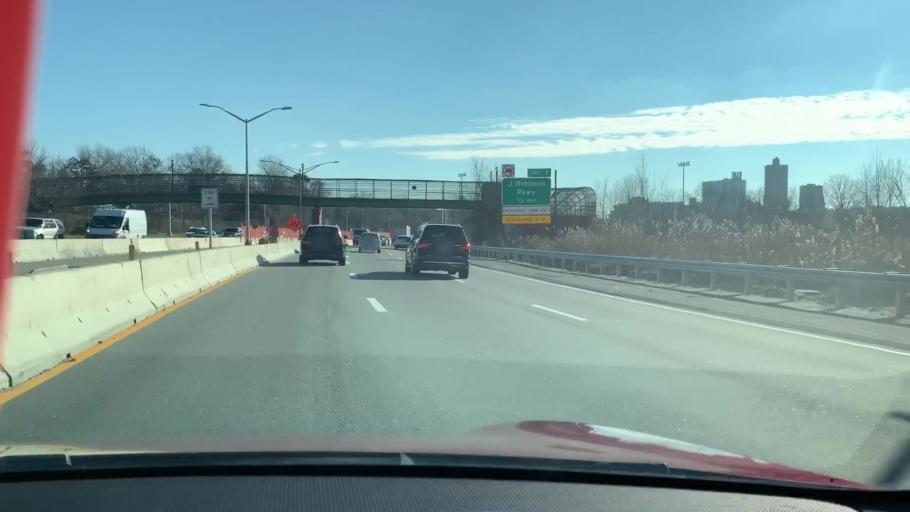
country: US
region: New York
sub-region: Queens County
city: Jamaica
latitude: 40.7236
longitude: -73.8284
